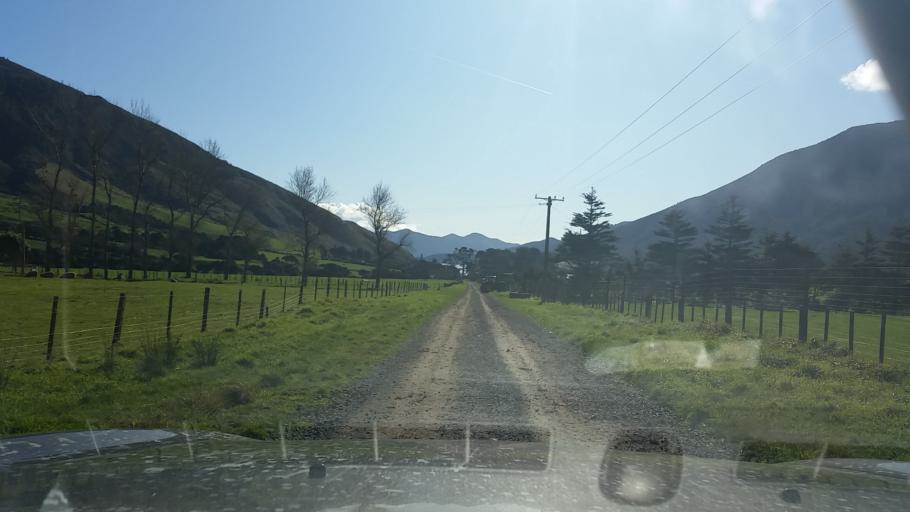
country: NZ
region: Marlborough
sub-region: Marlborough District
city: Picton
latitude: -41.1216
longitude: 174.0381
